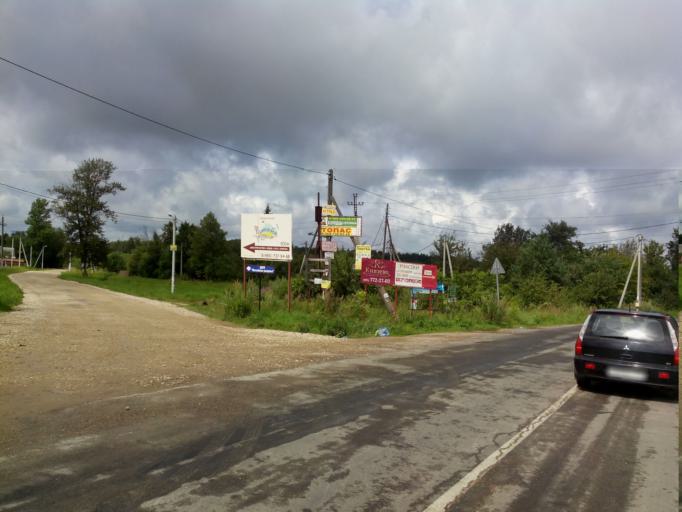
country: RU
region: Moskovskaya
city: Dorokhovo
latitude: 55.5117
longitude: 36.2171
